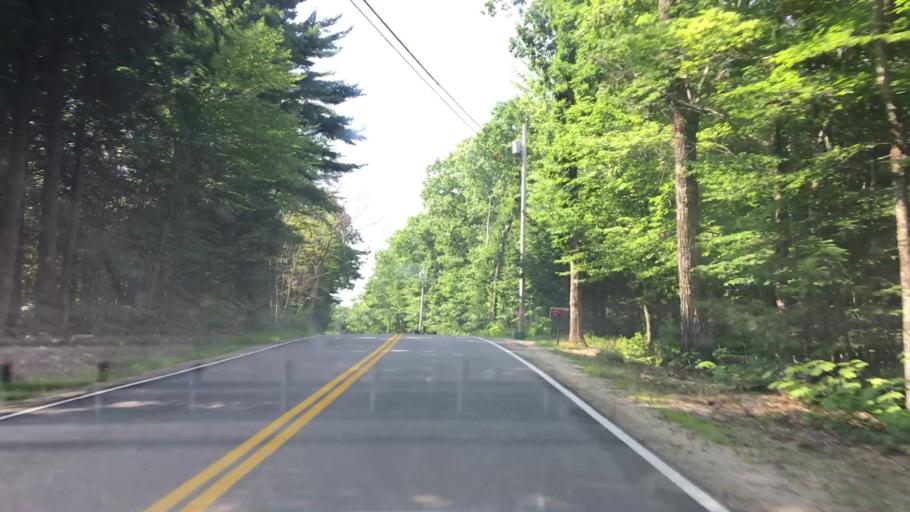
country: US
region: Maine
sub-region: Cumberland County
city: Raymond
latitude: 43.9648
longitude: -70.4139
